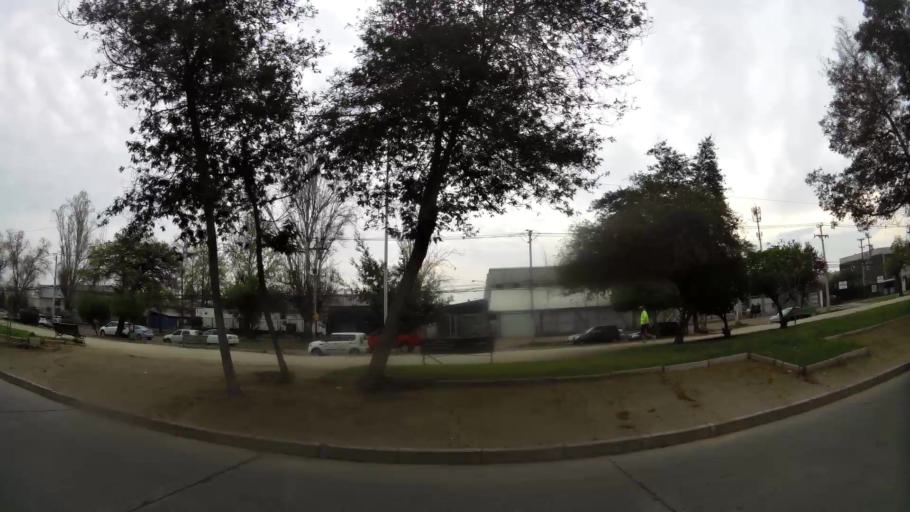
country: CL
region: Santiago Metropolitan
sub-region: Provincia de Santiago
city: Villa Presidente Frei, Nunoa, Santiago, Chile
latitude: -33.4821
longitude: -70.6129
